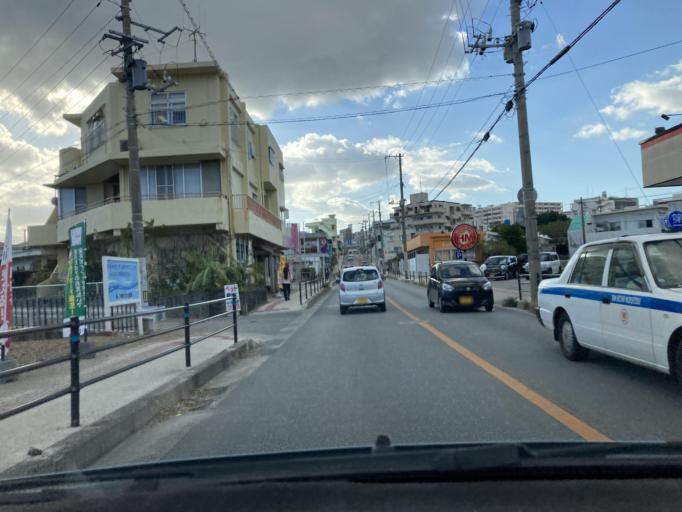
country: JP
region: Okinawa
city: Okinawa
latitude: 26.3331
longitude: 127.8135
